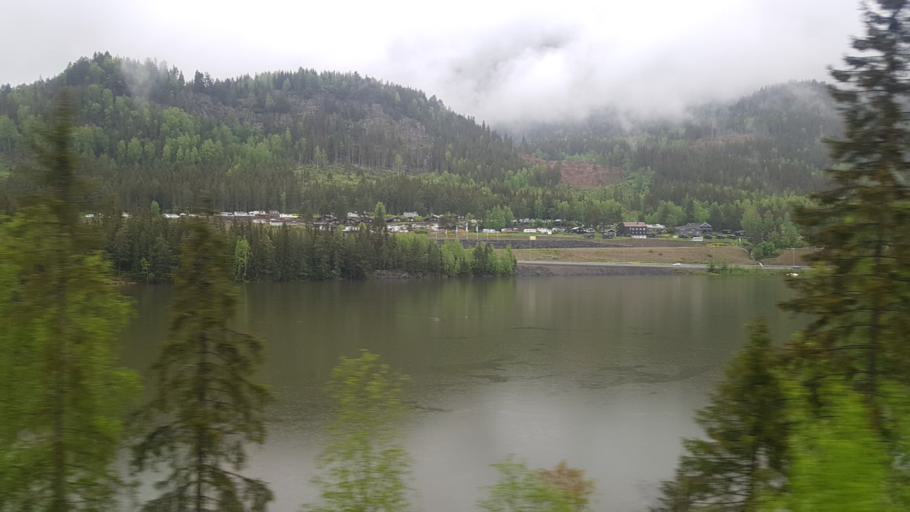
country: NO
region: Oppland
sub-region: Oyer
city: Tretten
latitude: 61.2708
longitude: 10.3855
